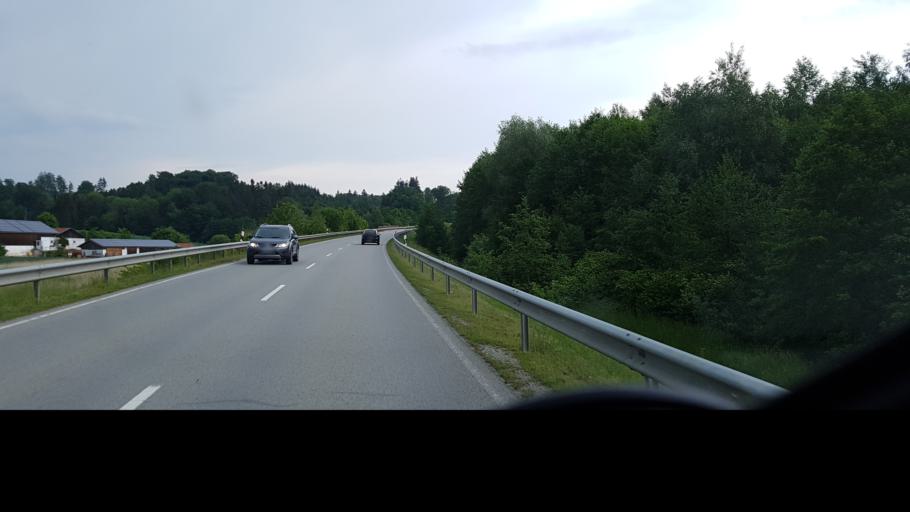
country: DE
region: Bavaria
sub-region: Lower Bavaria
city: Bad Griesbach
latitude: 48.4657
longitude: 13.1907
